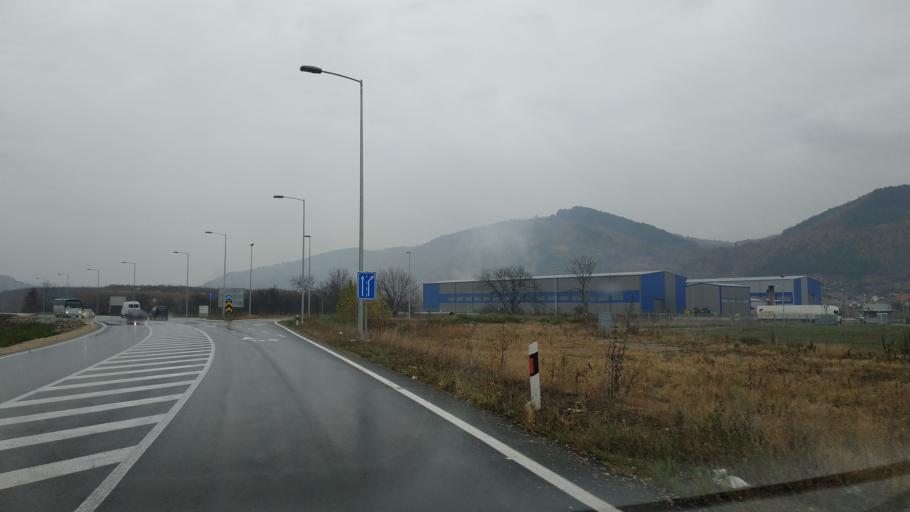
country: RS
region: Central Serbia
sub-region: Pirotski Okrug
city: Pirot
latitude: 43.1779
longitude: 22.5717
